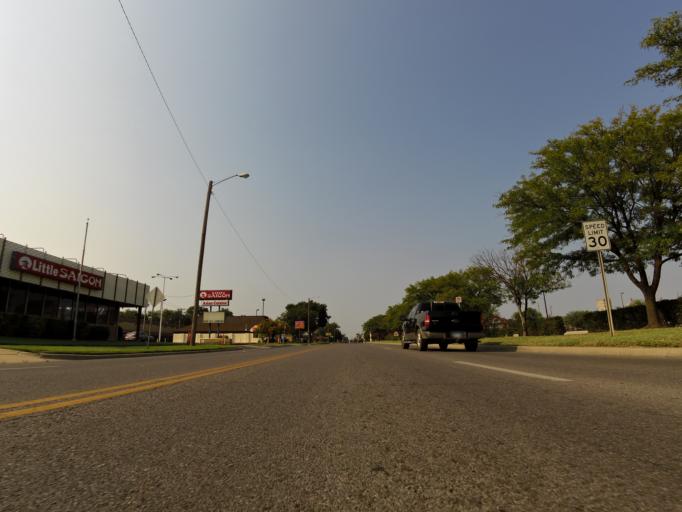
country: US
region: Kansas
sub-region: Sedgwick County
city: Wichita
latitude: 37.7006
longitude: -97.3356
